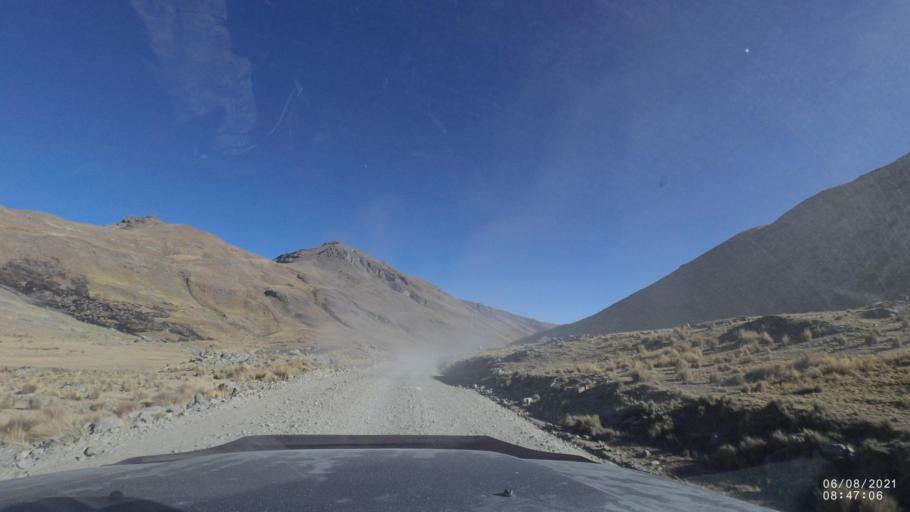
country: BO
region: Cochabamba
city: Sipe Sipe
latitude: -17.1661
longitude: -66.4241
